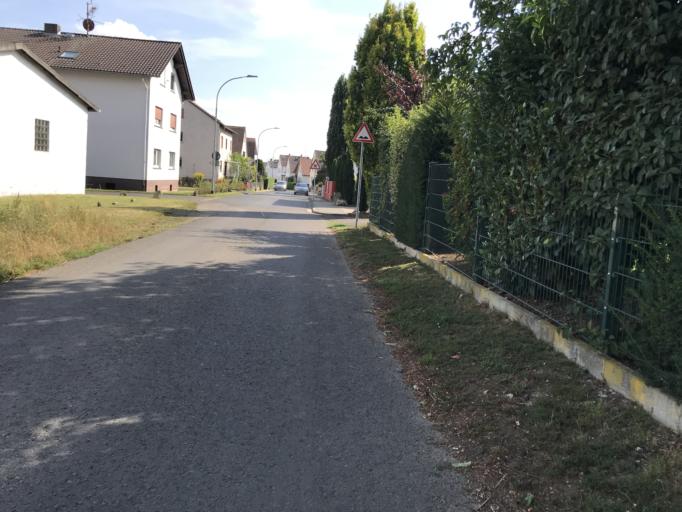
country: DE
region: Hesse
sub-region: Regierungsbezirk Darmstadt
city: Wolfersheim
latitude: 50.3658
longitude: 8.8224
